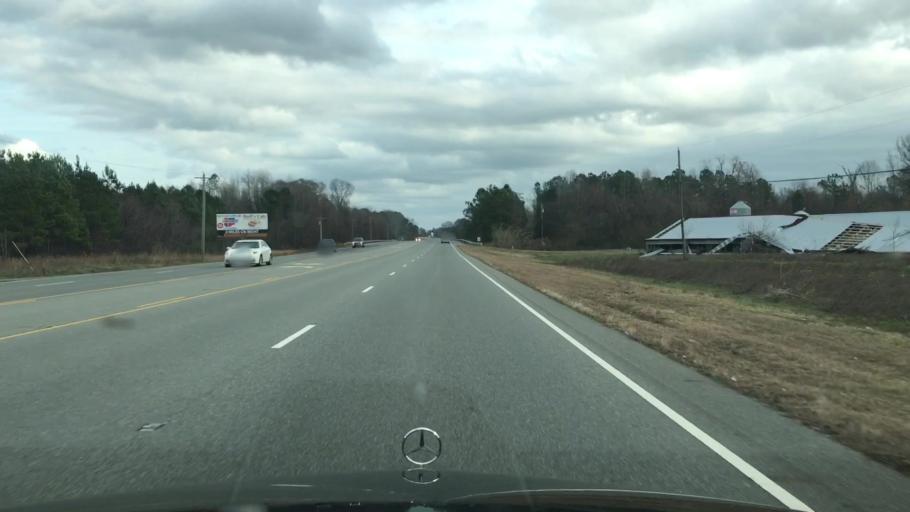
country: US
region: North Carolina
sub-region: Duplin County
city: Beulaville
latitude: 34.9286
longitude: -77.8061
